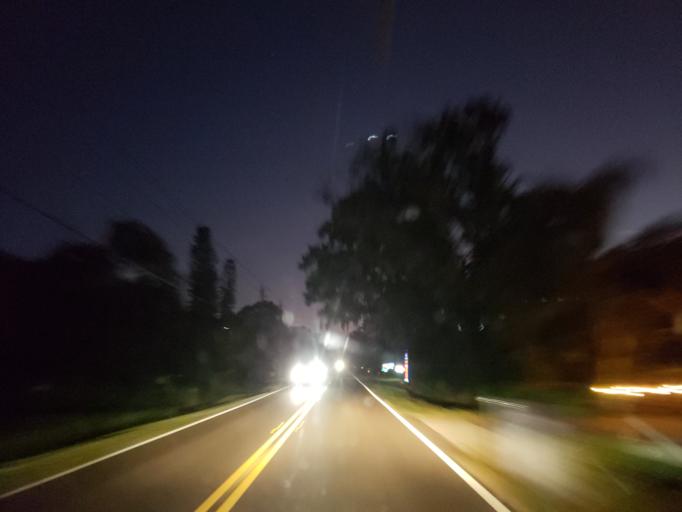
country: US
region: Florida
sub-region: Hillsborough County
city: Dover
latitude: 27.9795
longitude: -82.2198
